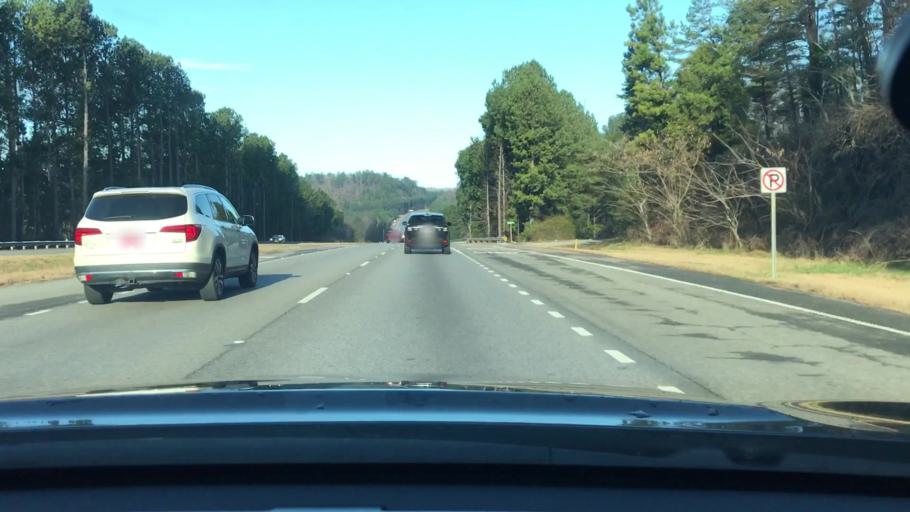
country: US
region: Alabama
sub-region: Shelby County
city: Chelsea
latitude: 33.3504
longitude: -86.6431
